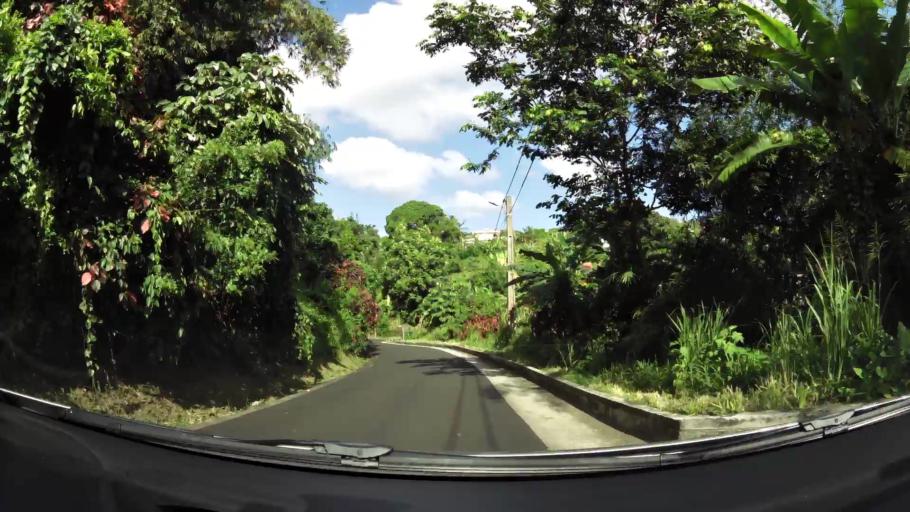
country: MQ
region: Martinique
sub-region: Martinique
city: La Trinite
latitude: 14.7362
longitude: -60.9742
